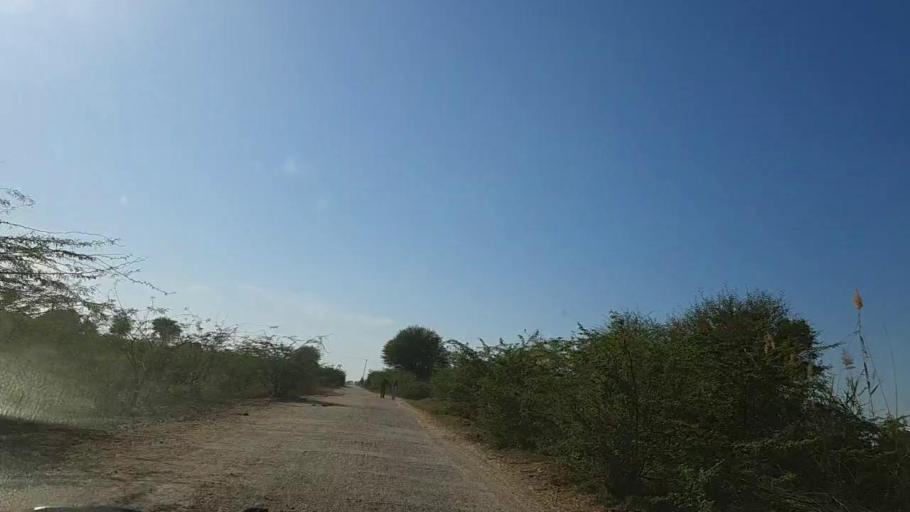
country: PK
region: Sindh
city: Dhoro Naro
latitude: 25.5039
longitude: 69.5460
